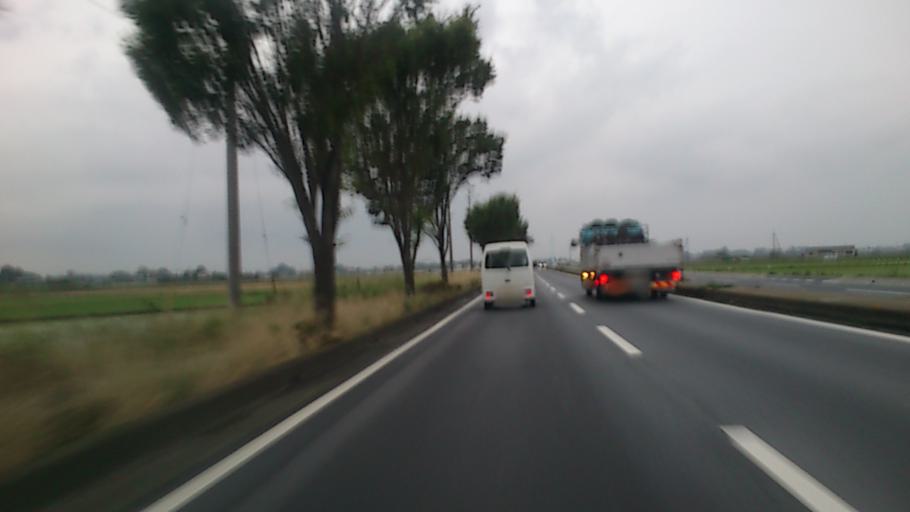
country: JP
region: Saitama
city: Hanyu
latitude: 36.1537
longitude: 139.5047
